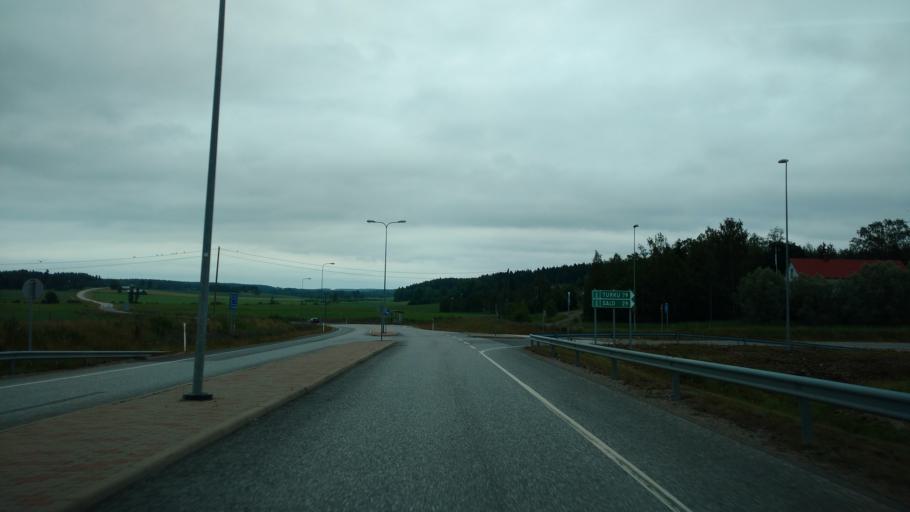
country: FI
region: Varsinais-Suomi
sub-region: Salo
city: Suomusjaervi
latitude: 60.3900
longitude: 23.5856
